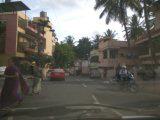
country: IN
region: Karnataka
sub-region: Bangalore Urban
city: Bangalore
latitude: 12.9850
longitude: 77.5377
